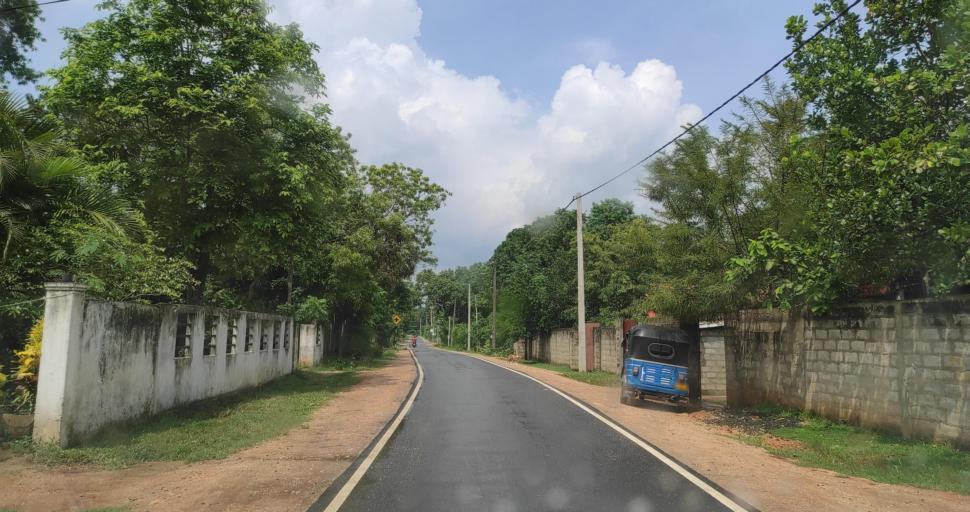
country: LK
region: Eastern Province
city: Trincomalee
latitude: 8.3714
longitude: 81.0126
